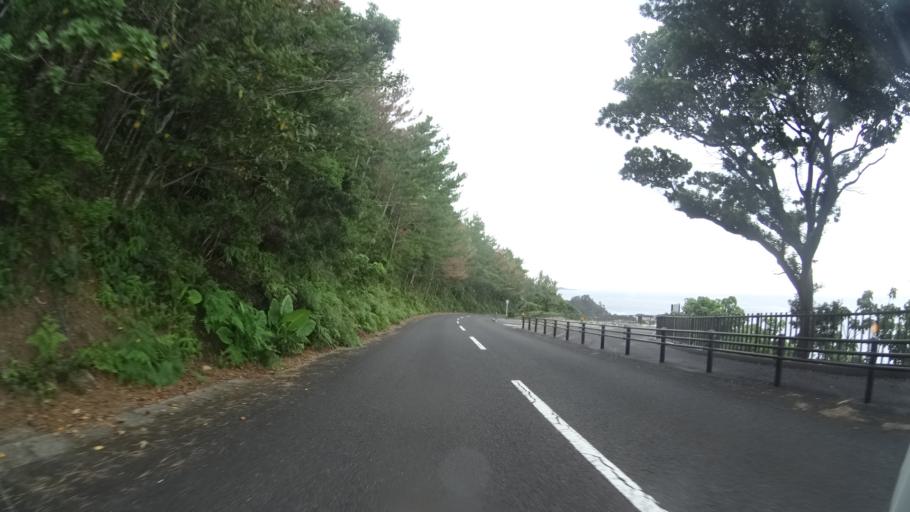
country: JP
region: Kagoshima
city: Nishinoomote
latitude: 30.3080
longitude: 130.4072
